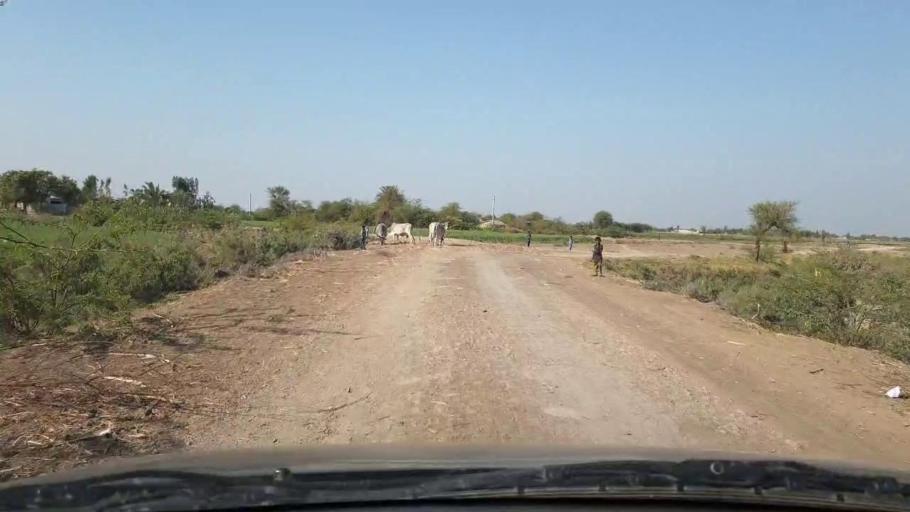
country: PK
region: Sindh
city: Samaro
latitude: 25.1764
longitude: 69.2834
